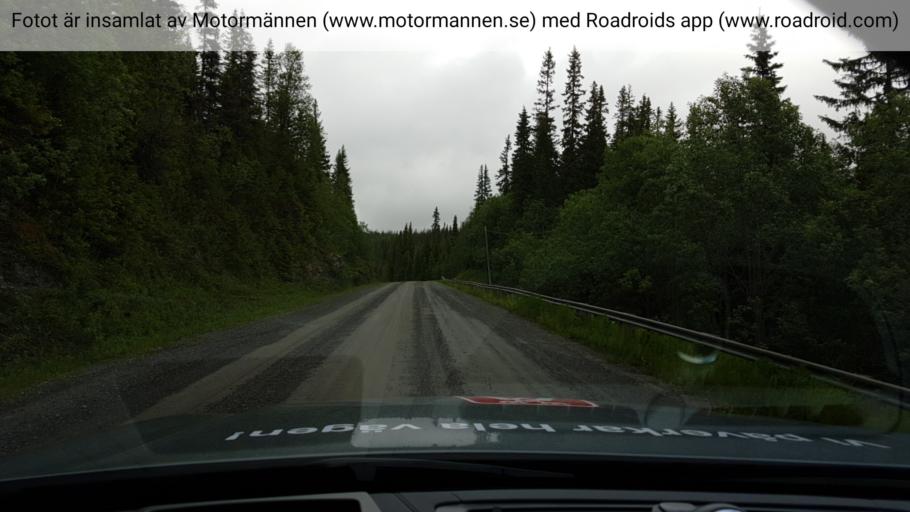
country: SE
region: Jaemtland
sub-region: Are Kommun
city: Are
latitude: 63.7206
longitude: 12.6077
